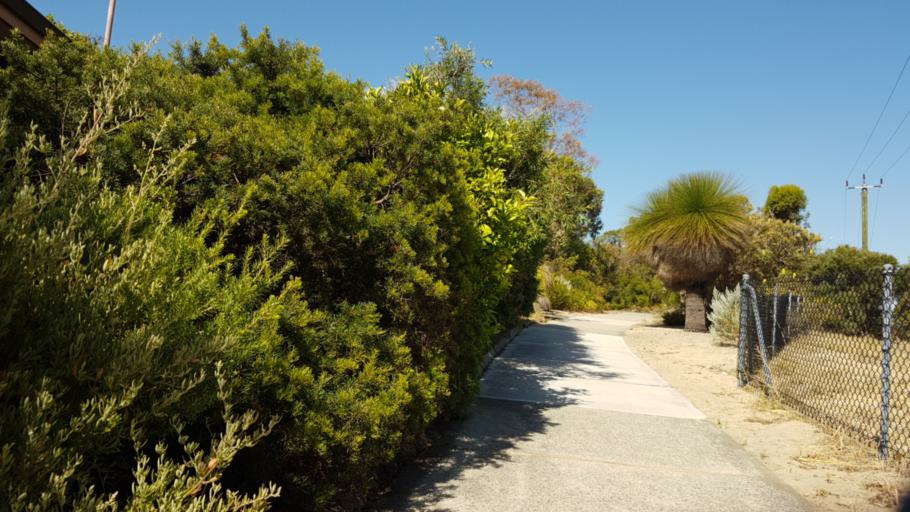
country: AU
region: Western Australia
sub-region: Stirling
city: Karrinyup
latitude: -31.8570
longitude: 115.7720
